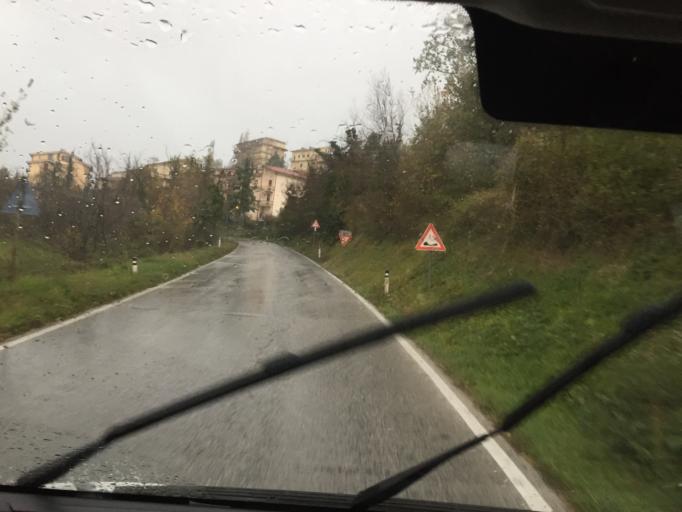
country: IT
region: The Marches
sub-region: Provincia di Macerata
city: Camerino
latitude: 43.1273
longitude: 13.0604
